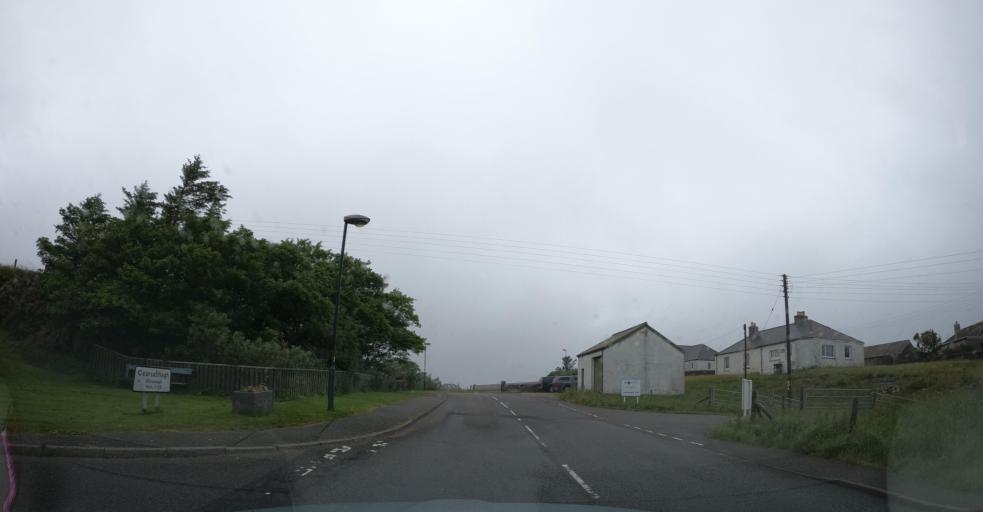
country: GB
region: Scotland
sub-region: Eilean Siar
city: Isle of North Uist
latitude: 57.6001
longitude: -7.1610
